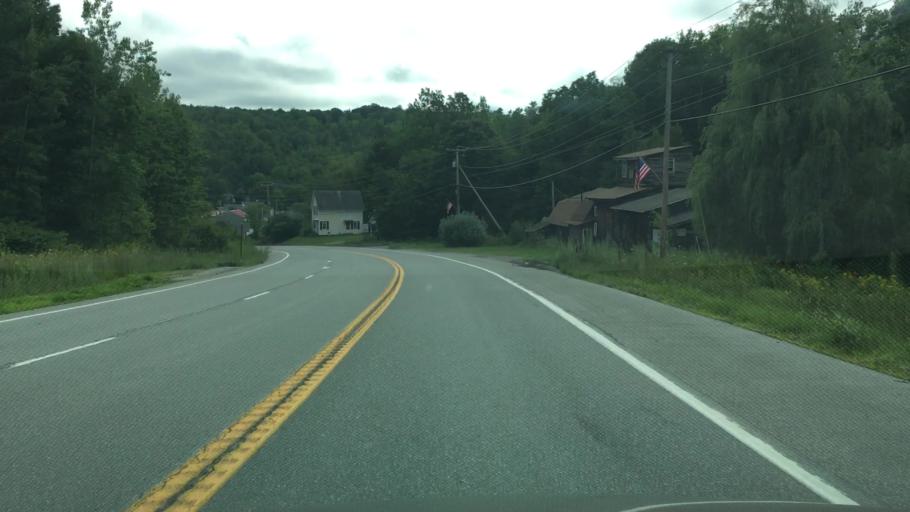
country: US
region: Maine
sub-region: Waldo County
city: Frankfort
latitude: 44.6114
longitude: -68.8714
